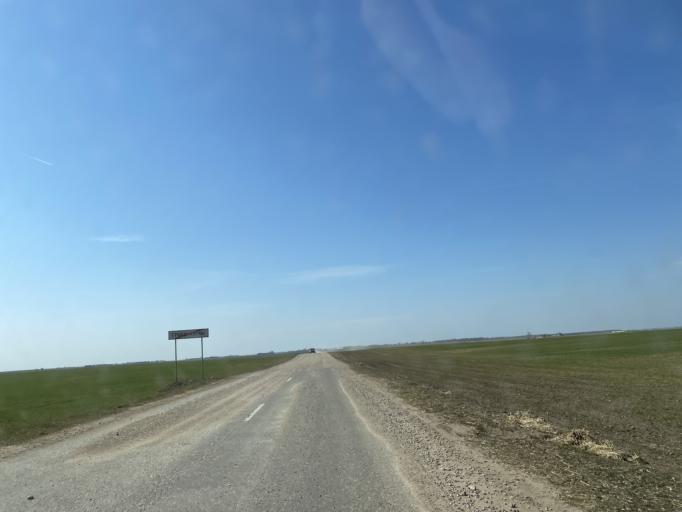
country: BY
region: Minsk
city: Snow
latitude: 53.1460
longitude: 26.4095
